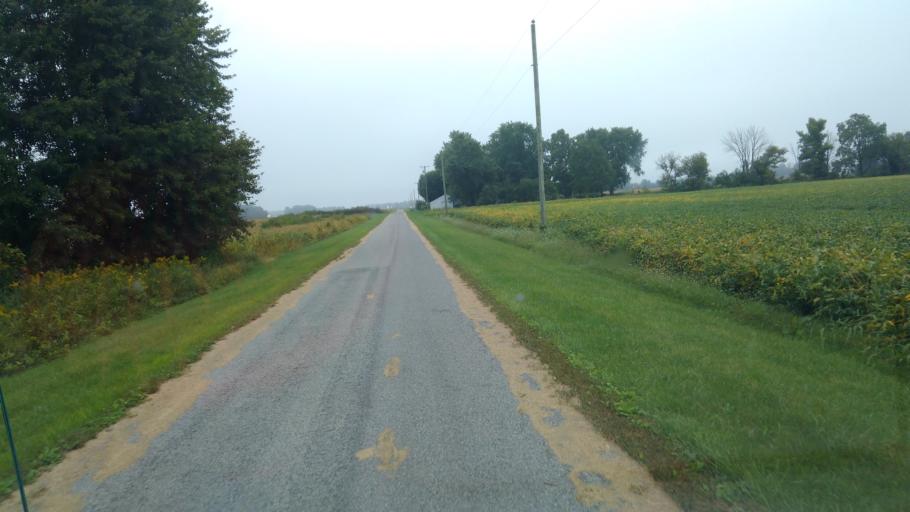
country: US
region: Ohio
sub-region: Union County
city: Richwood
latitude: 40.5007
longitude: -83.3647
